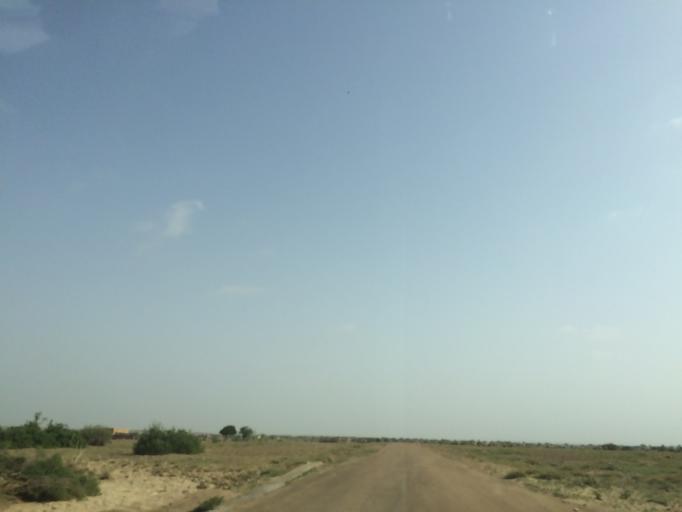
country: IN
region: Rajasthan
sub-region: Jaisalmer
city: Jaisalmer
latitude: 26.7972
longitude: 70.6911
